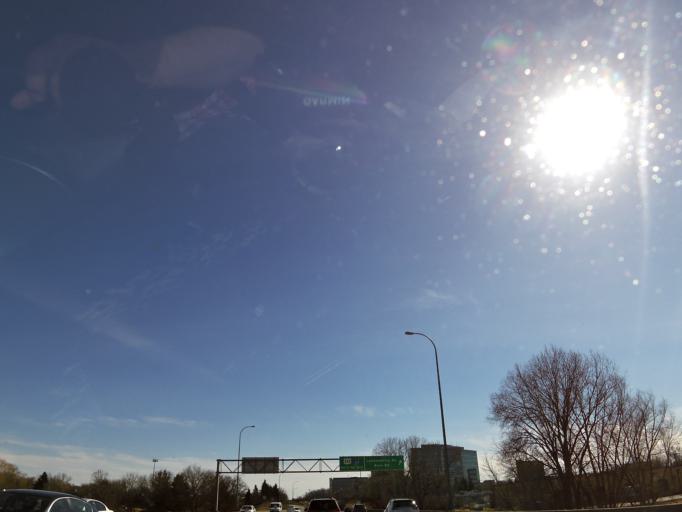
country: US
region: Minnesota
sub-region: Hennepin County
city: Edina
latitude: 44.9053
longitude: -93.4015
